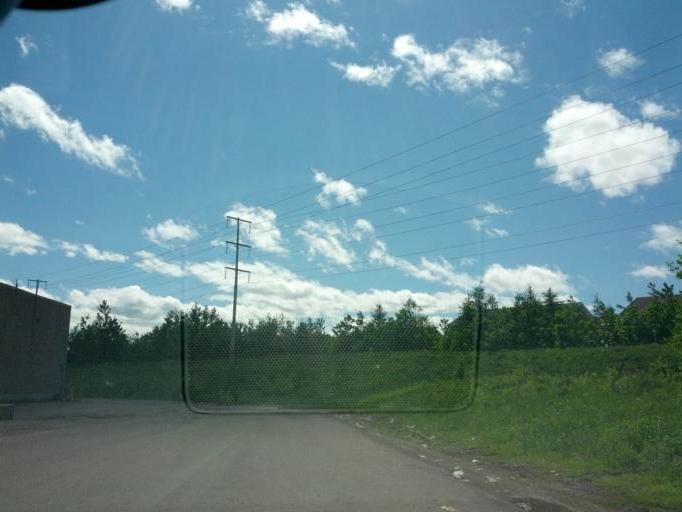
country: CA
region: New Brunswick
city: Moncton
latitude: 46.1191
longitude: -64.8327
